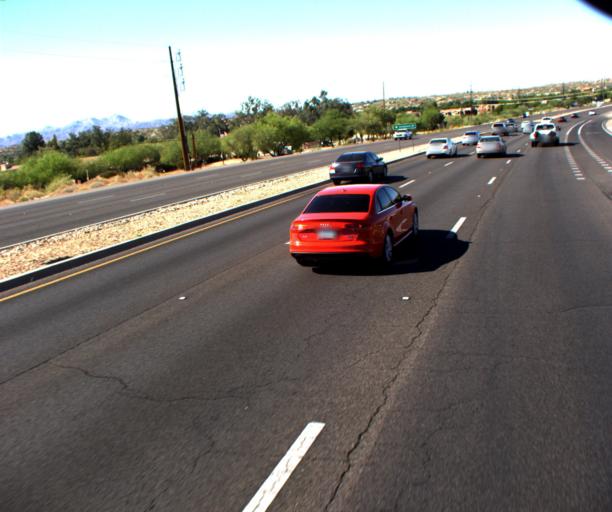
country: US
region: Arizona
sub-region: Pima County
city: Oro Valley
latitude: 32.3899
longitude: -110.9639
